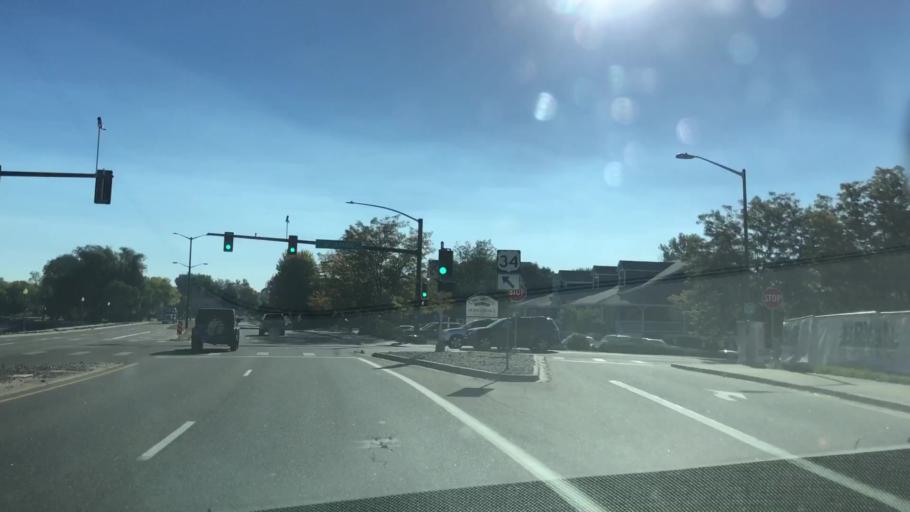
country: US
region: Colorado
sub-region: Larimer County
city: Loveland
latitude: 40.4046
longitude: -105.0878
